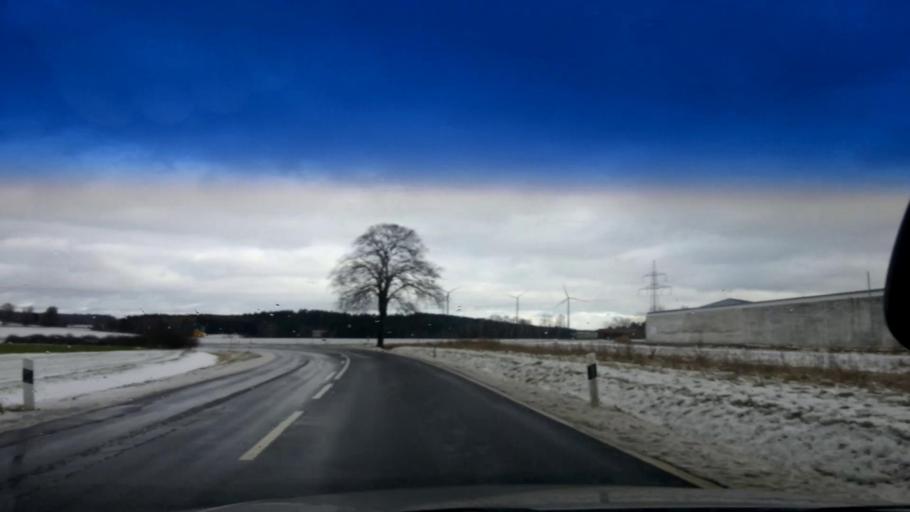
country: DE
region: Bavaria
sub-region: Upper Franconia
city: Marktleuthen
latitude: 50.1362
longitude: 12.0107
